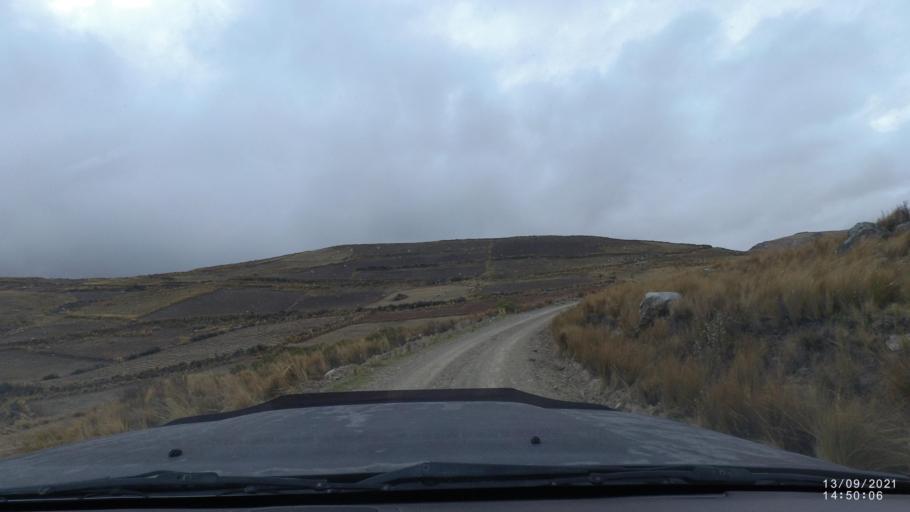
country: BO
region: Cochabamba
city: Colomi
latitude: -17.3483
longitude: -65.7965
